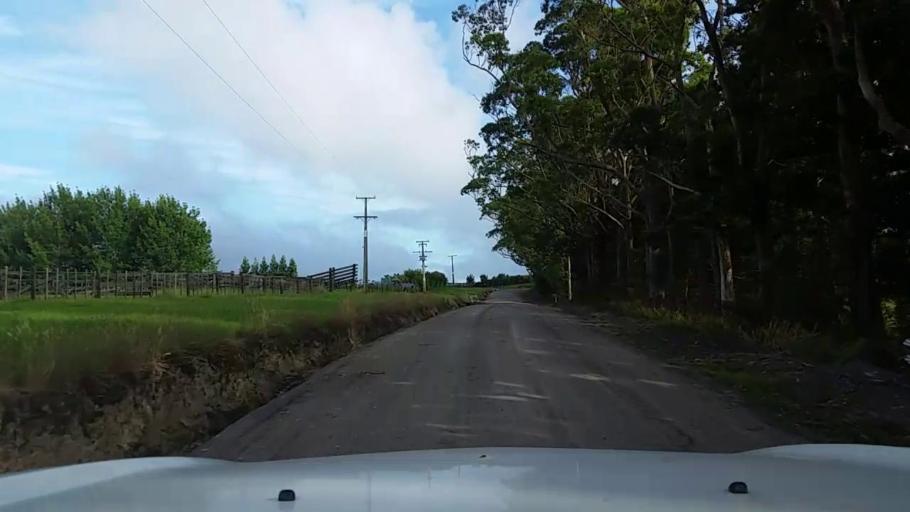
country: NZ
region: Northland
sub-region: Whangarei
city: Maungatapere
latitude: -35.6724
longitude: 174.1753
